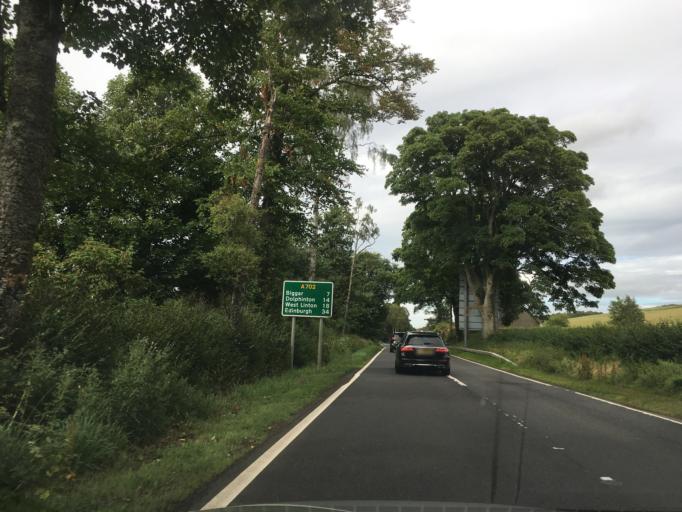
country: GB
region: Scotland
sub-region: South Lanarkshire
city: Biggar
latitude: 55.5552
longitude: -3.6318
